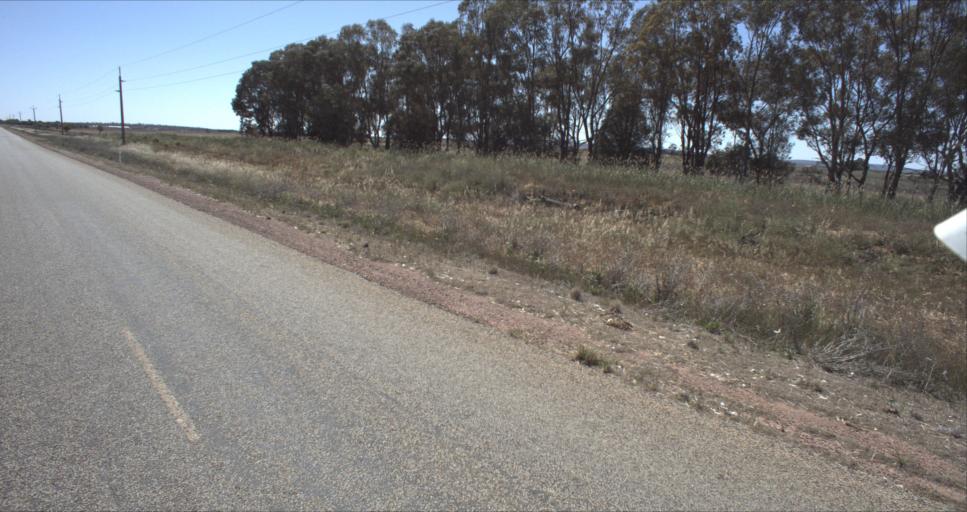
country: AU
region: New South Wales
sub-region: Leeton
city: Leeton
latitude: -34.4644
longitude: 146.2935
